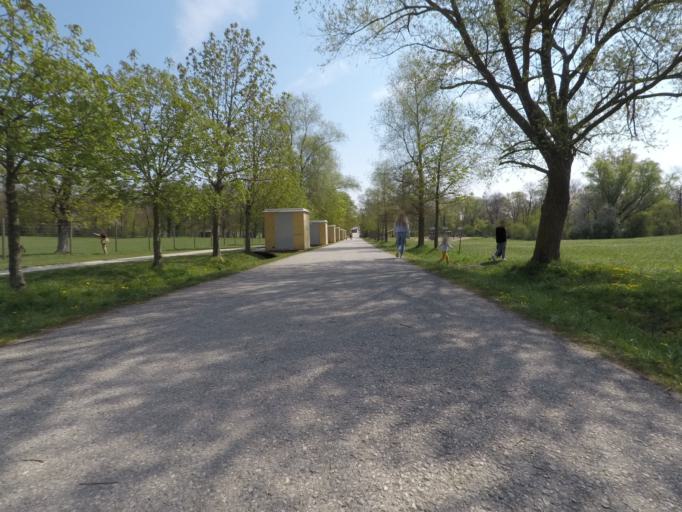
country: AT
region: Lower Austria
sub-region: Politischer Bezirk Modling
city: Perchtoldsdorf
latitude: 48.1670
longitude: 16.2529
